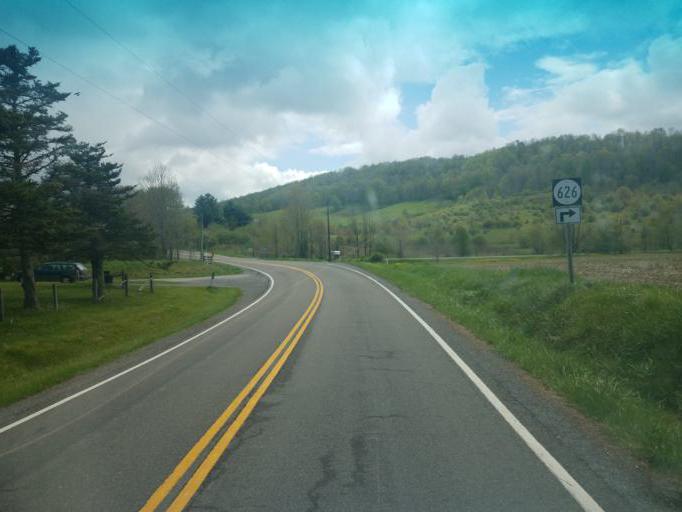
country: US
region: Virginia
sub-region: Wythe County
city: Rural Retreat
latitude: 37.0074
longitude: -81.3622
